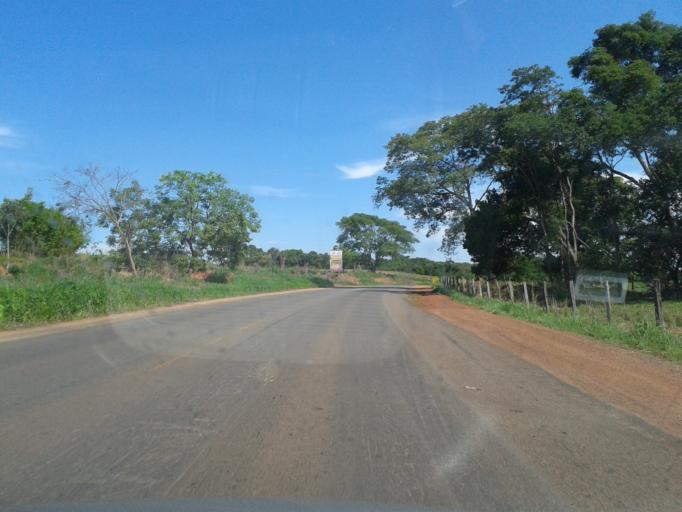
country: BR
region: Goias
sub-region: Piracanjuba
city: Piracanjuba
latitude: -17.2287
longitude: -48.7133
